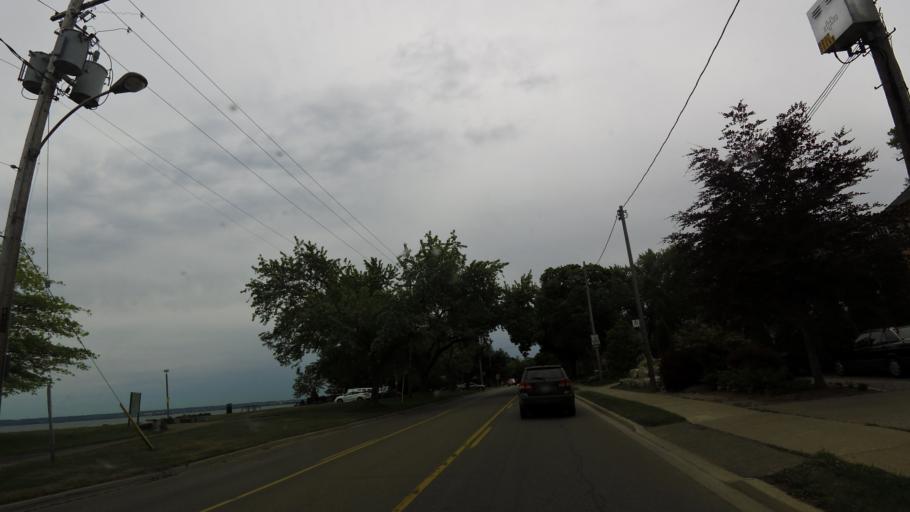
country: CA
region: Ontario
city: Burlington
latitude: 43.3385
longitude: -79.7698
